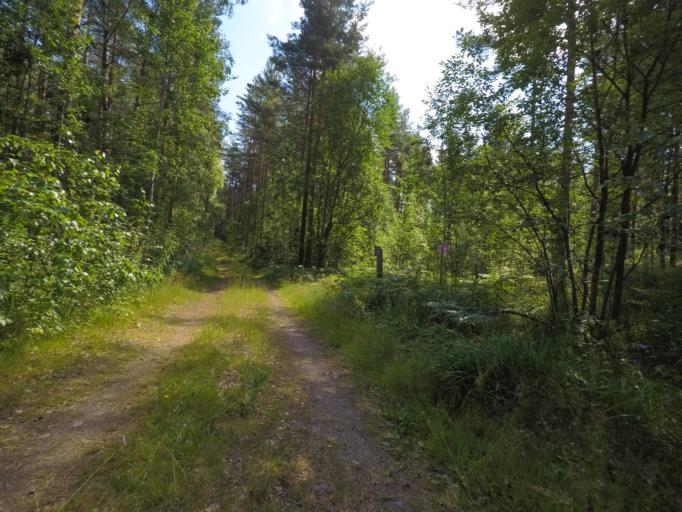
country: FI
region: Southern Savonia
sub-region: Mikkeli
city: Puumala
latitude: 61.5161
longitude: 28.1670
